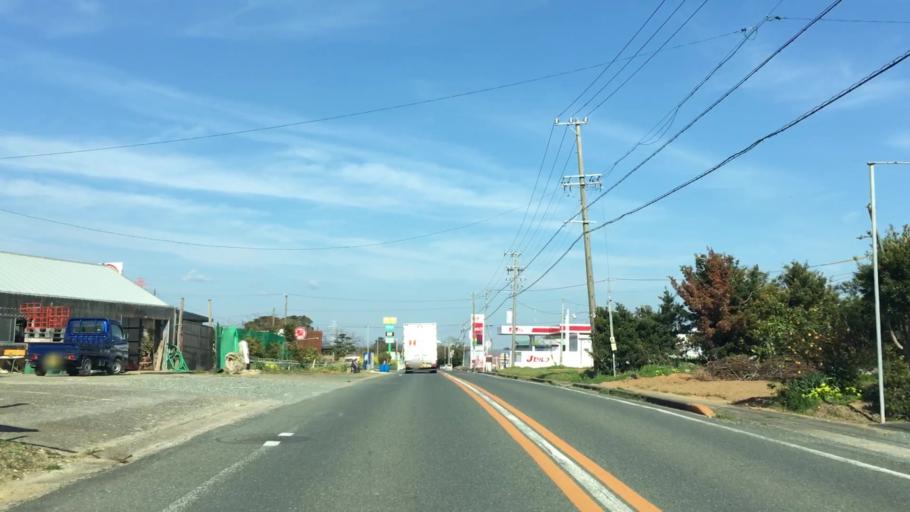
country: JP
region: Shizuoka
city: Kosai-shi
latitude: 34.6825
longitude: 137.4484
